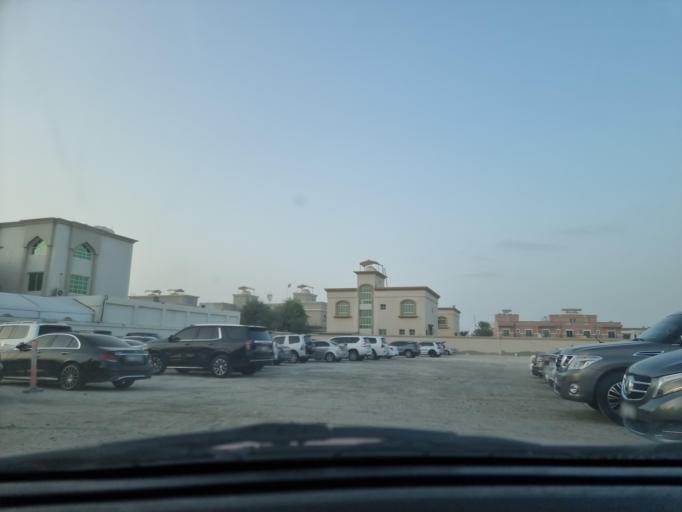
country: AE
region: Abu Dhabi
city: Abu Dhabi
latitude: 24.4067
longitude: 54.6026
